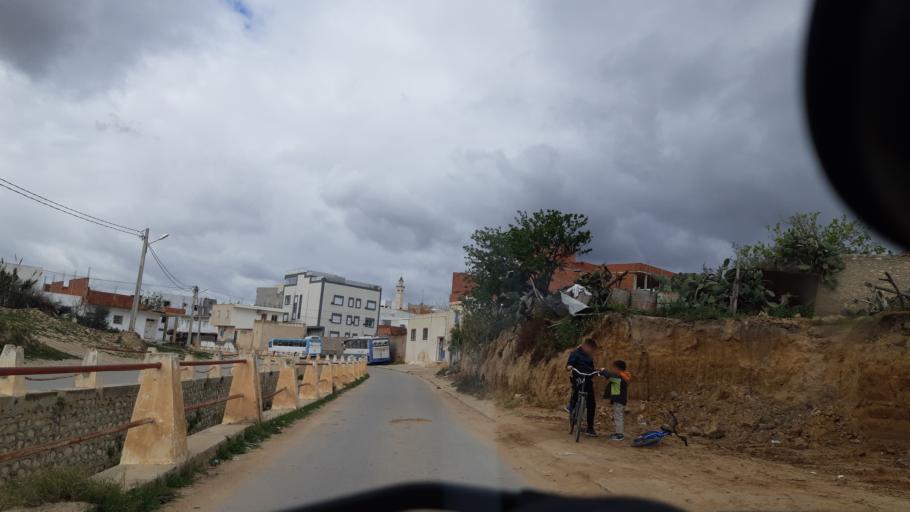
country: TN
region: Susah
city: Akouda
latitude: 35.8678
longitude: 10.5394
